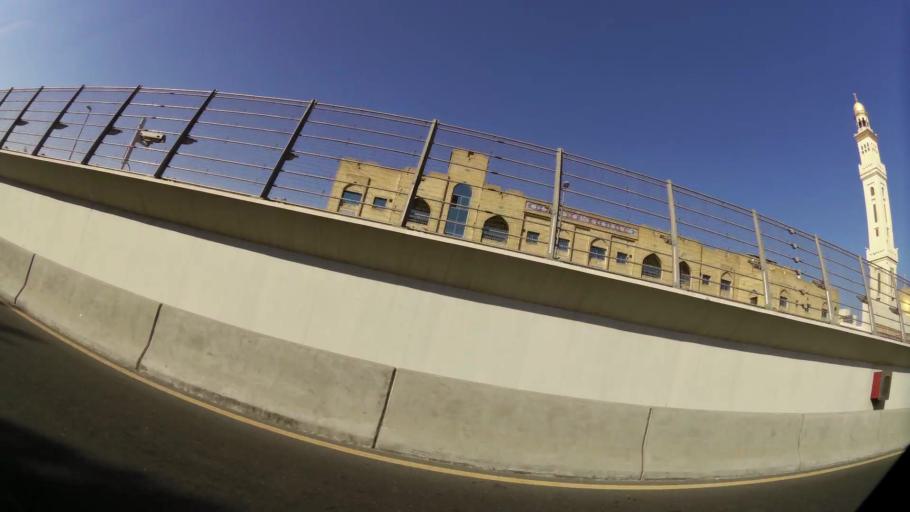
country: AE
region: Ash Shariqah
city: Sharjah
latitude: 25.2536
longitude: 55.3068
